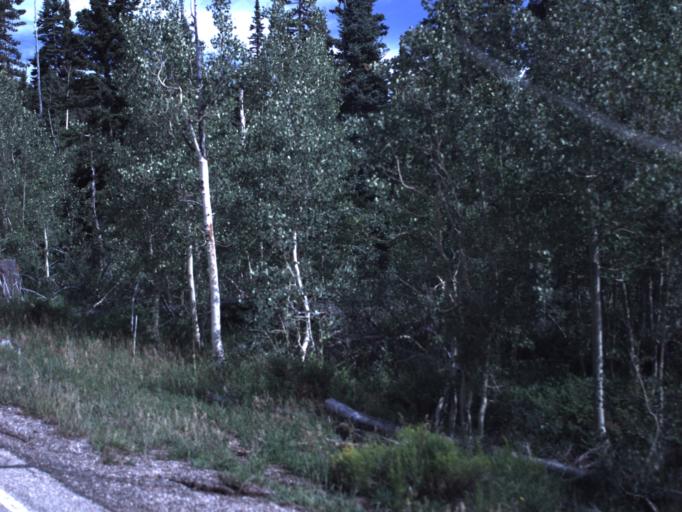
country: US
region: Utah
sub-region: Iron County
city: Parowan
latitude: 37.5191
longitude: -112.7047
